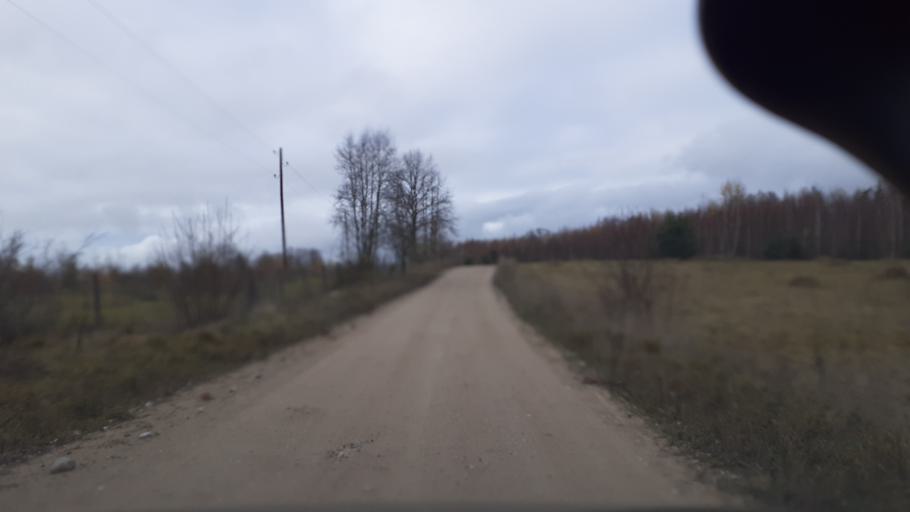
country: LV
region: Kuldigas Rajons
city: Kuldiga
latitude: 57.0411
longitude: 21.8772
